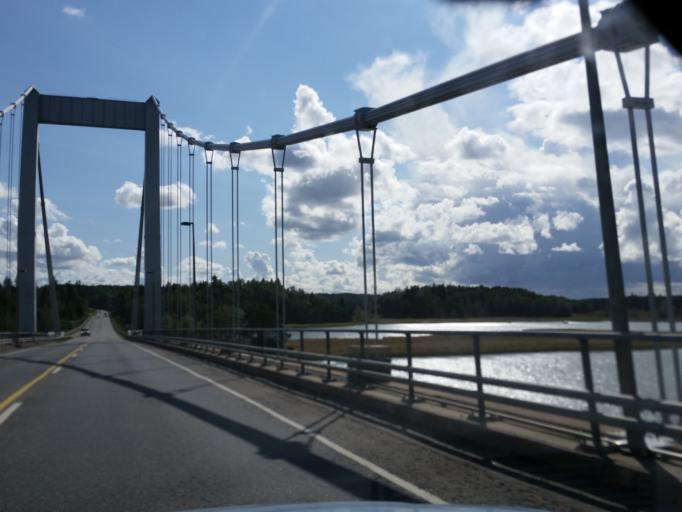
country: FI
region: Varsinais-Suomi
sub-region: Turku
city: Kaarina
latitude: 60.3658
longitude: 22.3583
